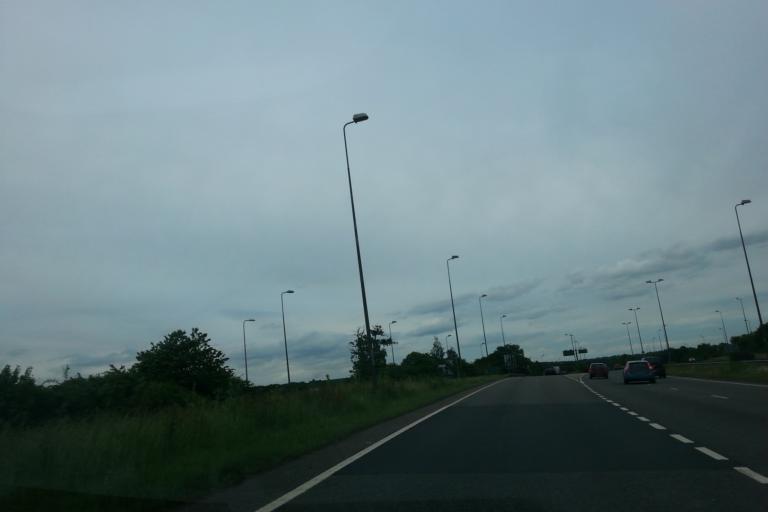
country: GB
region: England
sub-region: Solihull
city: Hampton in Arden
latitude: 52.4461
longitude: -1.6952
